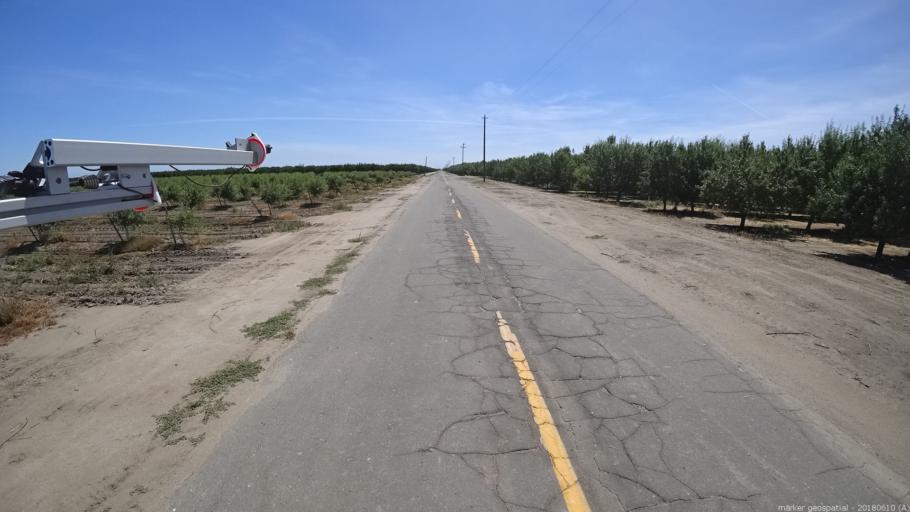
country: US
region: California
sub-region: Madera County
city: Chowchilla
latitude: 37.0399
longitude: -120.3662
